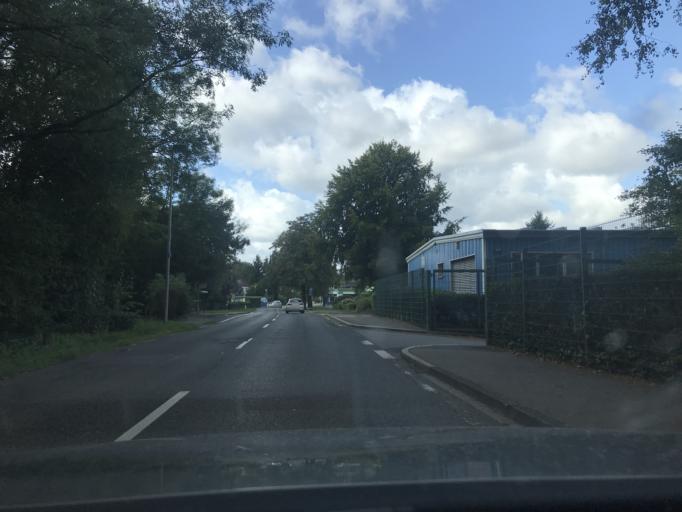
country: DE
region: North Rhine-Westphalia
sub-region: Regierungsbezirk Dusseldorf
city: Mettmann
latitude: 51.2160
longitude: 6.9692
